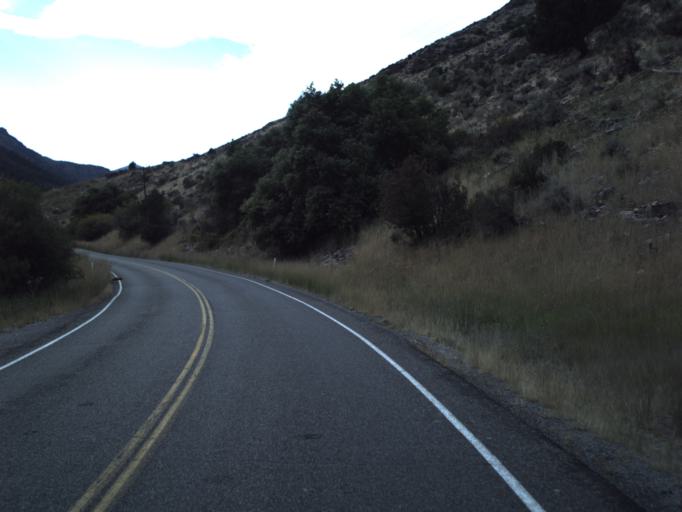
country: US
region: Utah
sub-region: Cache County
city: Millville
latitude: 41.6079
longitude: -111.6101
